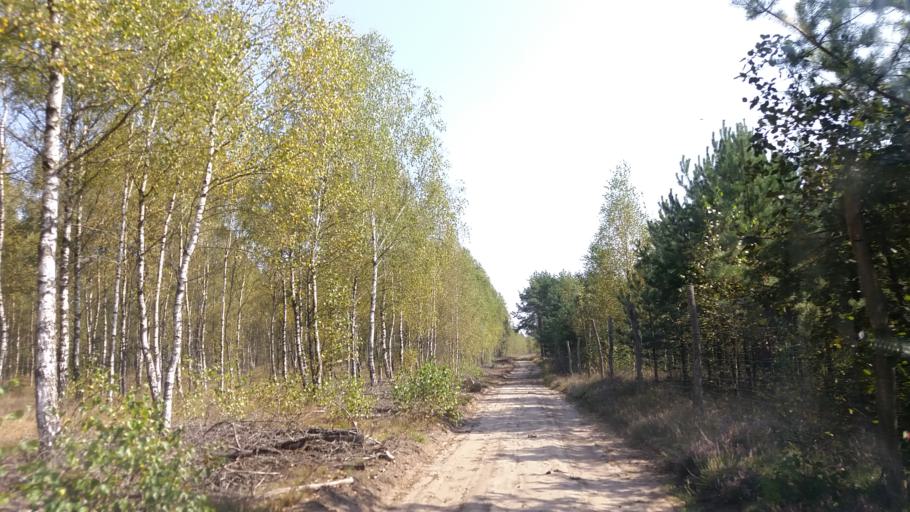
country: PL
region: West Pomeranian Voivodeship
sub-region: Powiat drawski
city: Kalisz Pomorski
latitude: 53.1371
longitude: 15.9393
